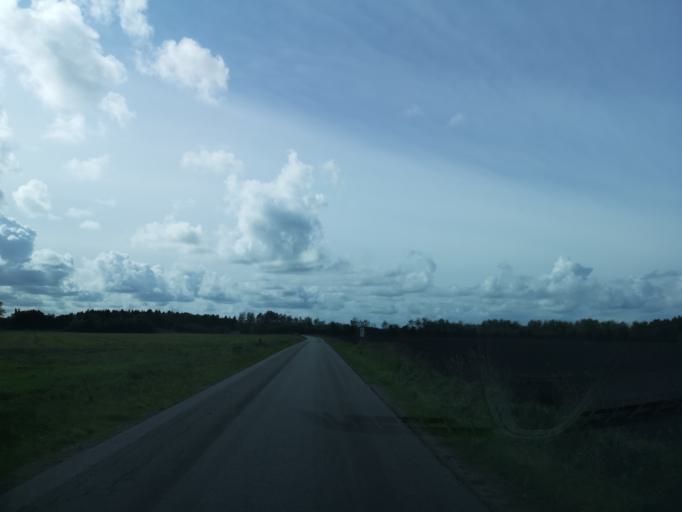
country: DK
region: Central Jutland
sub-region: Ringkobing-Skjern Kommune
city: Skjern
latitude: 55.9455
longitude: 8.5335
